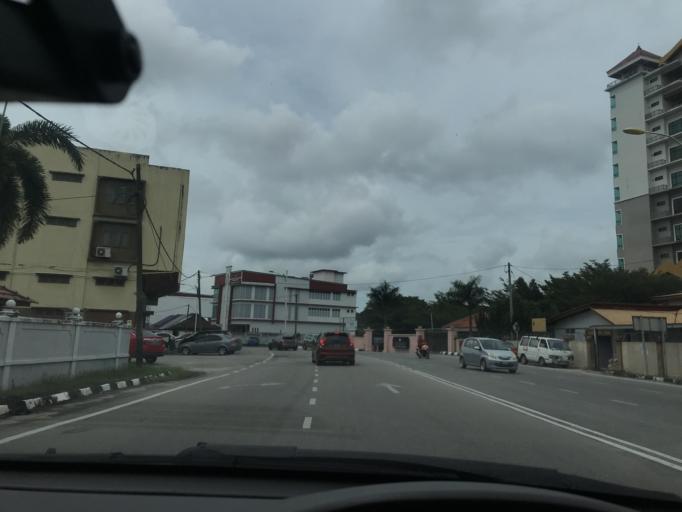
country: MY
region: Kelantan
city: Kota Bharu
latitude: 6.1112
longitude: 102.2378
